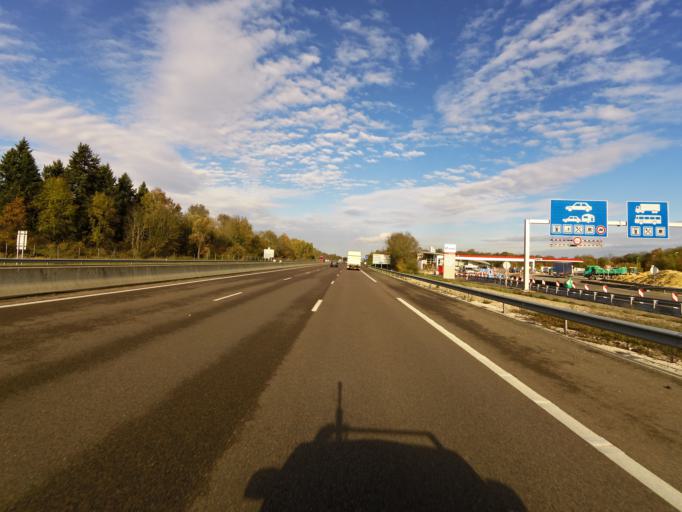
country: FR
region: Bourgogne
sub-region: Departement de la Cote-d'Or
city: Gevrey-Chambertin
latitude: 47.2216
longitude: 5.0078
